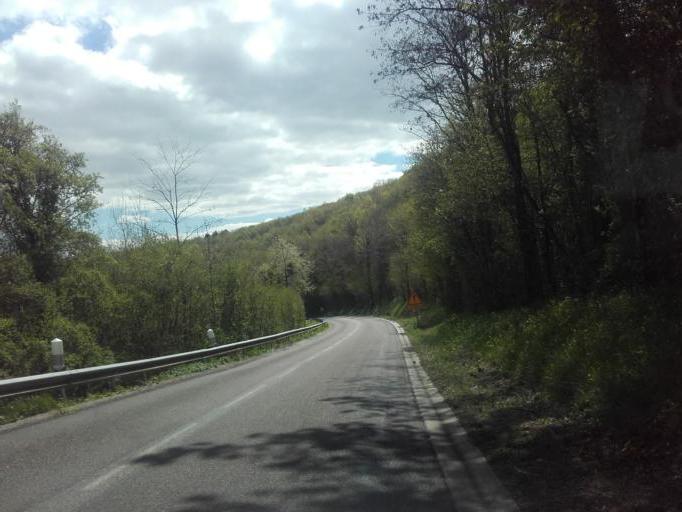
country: FR
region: Bourgogne
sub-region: Departement de la Cote-d'Or
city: Meursault
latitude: 47.0139
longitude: 4.7255
